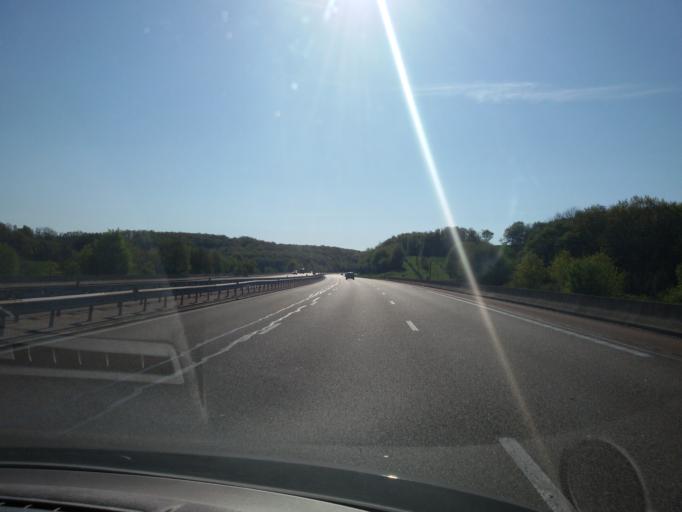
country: FR
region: Bourgogne
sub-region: Departement de l'Yonne
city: Cezy
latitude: 47.9280
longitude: 3.2627
